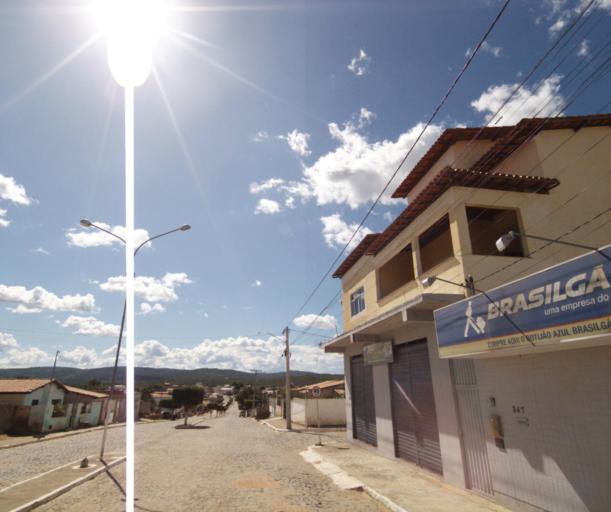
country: BR
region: Bahia
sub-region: Pocoes
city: Pocoes
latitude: -14.2419
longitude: -40.7667
